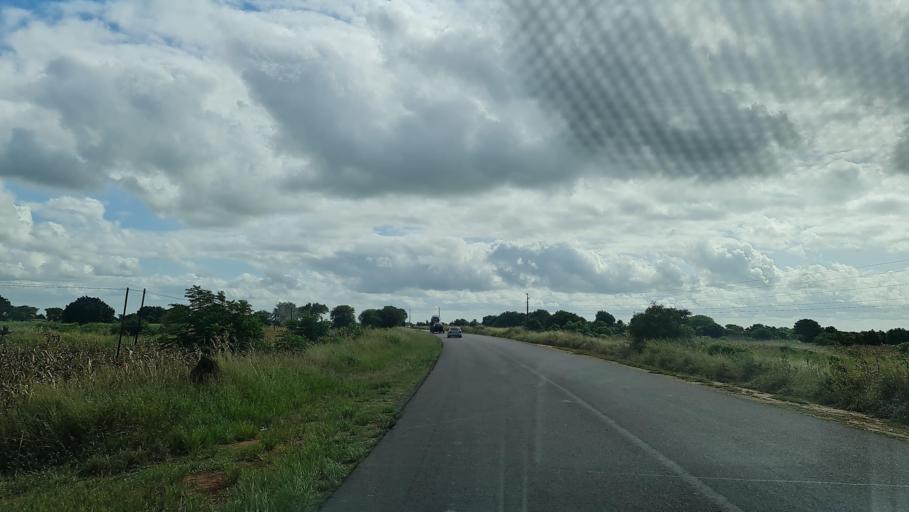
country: MZ
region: Gaza
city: Macia
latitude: -25.0886
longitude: 32.8429
